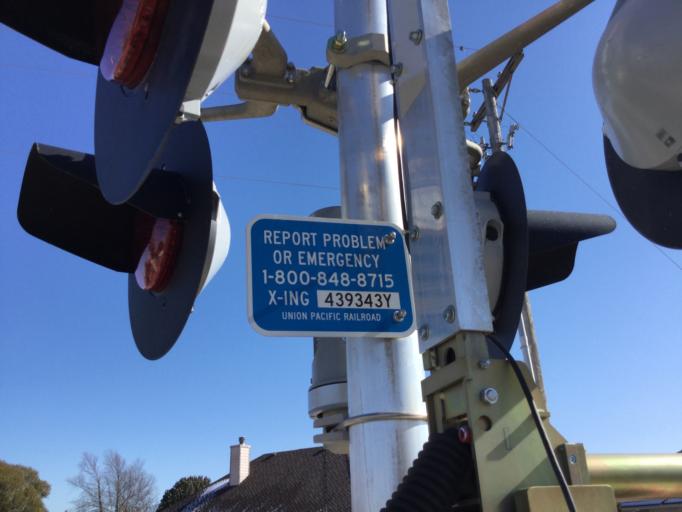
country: US
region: Kansas
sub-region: Sedgwick County
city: Bellaire
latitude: 37.7643
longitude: -97.2447
